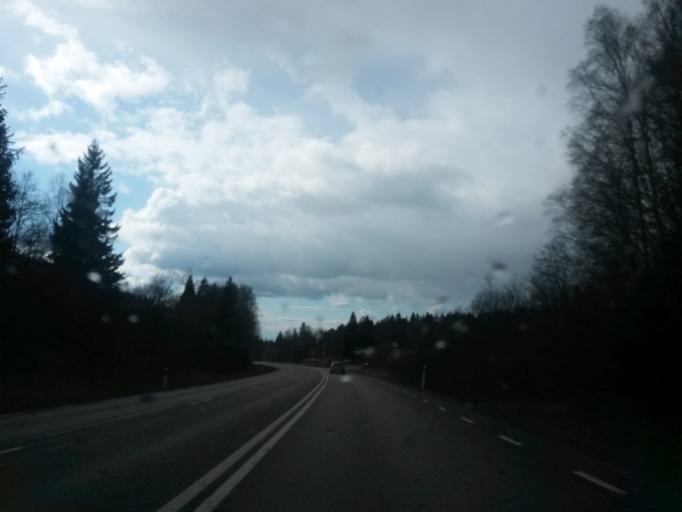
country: SE
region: Vaestra Goetaland
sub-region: Skovde Kommun
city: Skultorp
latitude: 58.3785
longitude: 13.7034
